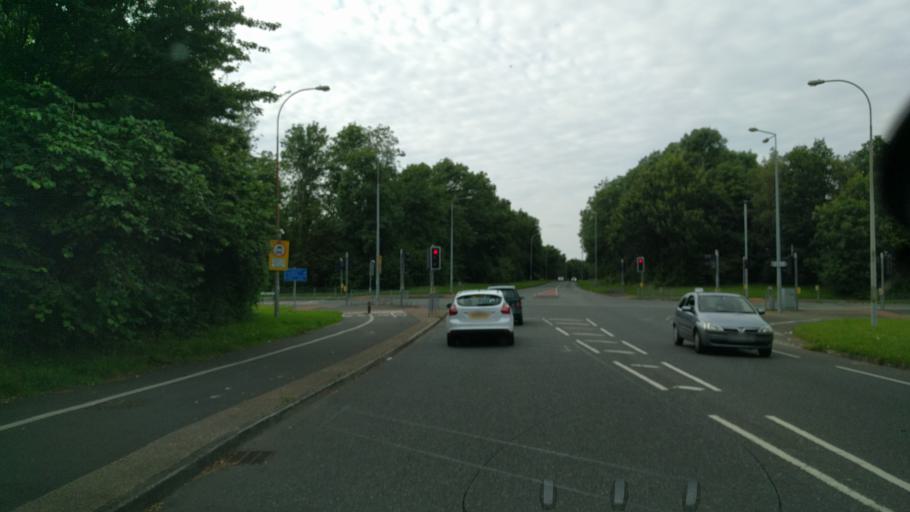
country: GB
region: England
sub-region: Warrington
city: Warrington
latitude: 53.4105
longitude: -2.5627
